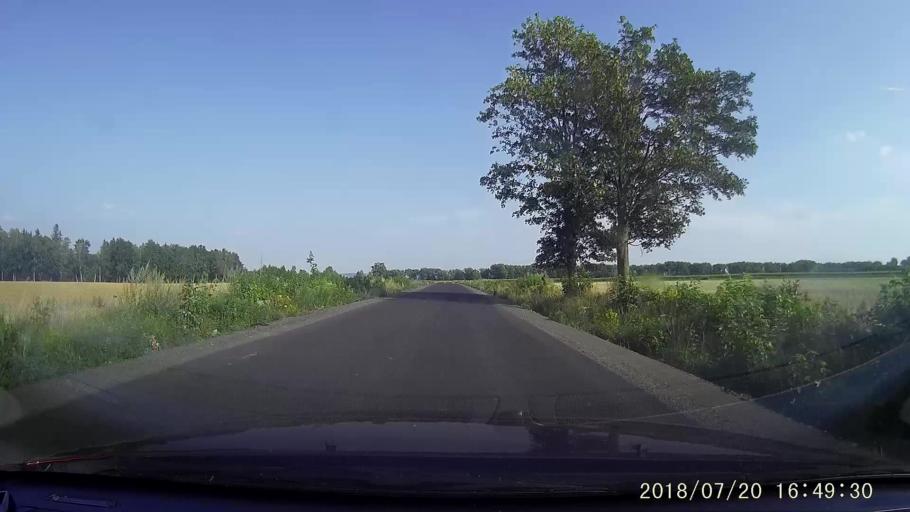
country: PL
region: Lower Silesian Voivodeship
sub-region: Powiat lubanski
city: Lesna
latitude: 51.0473
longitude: 15.1965
